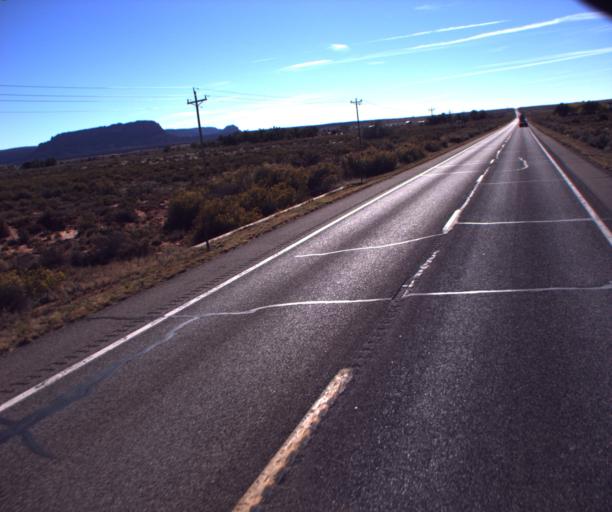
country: US
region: Arizona
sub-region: Mohave County
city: Colorado City
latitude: 36.9352
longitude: -112.9470
